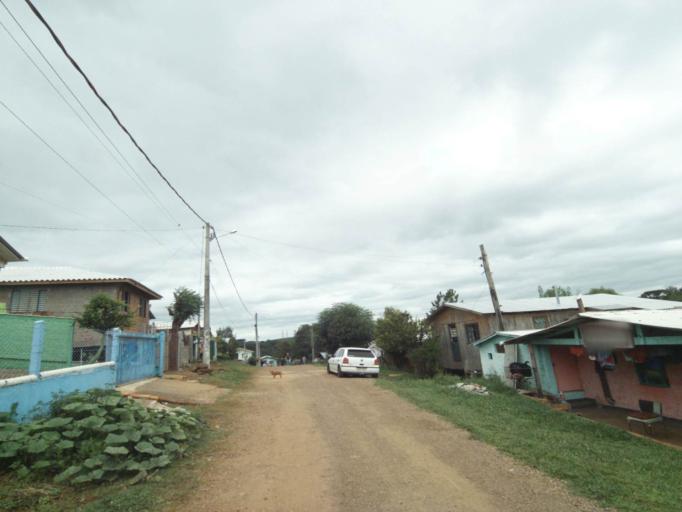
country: BR
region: Rio Grande do Sul
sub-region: Lagoa Vermelha
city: Lagoa Vermelha
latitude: -28.2144
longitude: -51.5066
